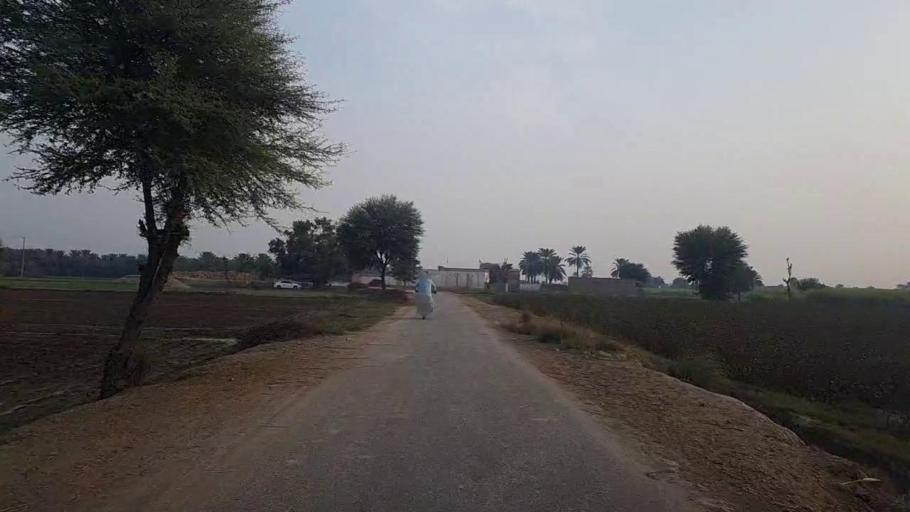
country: PK
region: Sindh
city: Kot Diji
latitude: 27.3844
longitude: 68.6609
